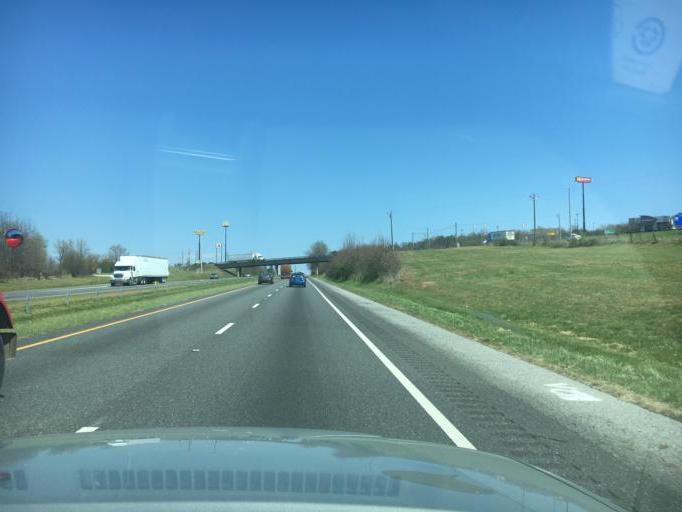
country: US
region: South Carolina
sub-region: Cherokee County
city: Blacksburg
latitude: 35.1396
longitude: -81.5113
